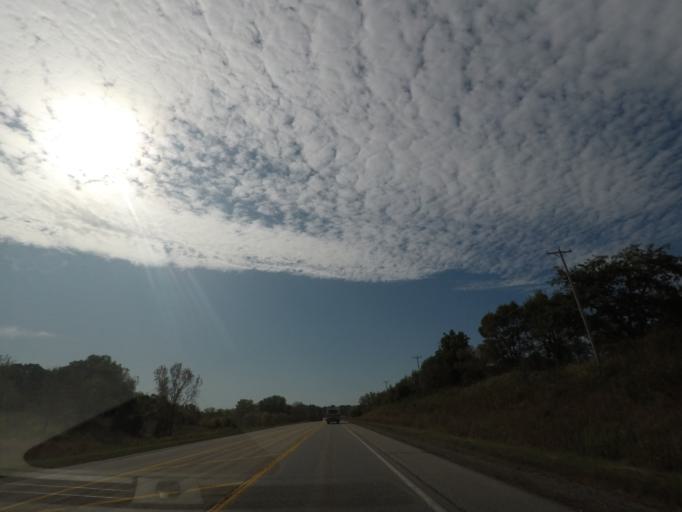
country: US
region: Iowa
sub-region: Story County
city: Ames
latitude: 42.0748
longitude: -93.6213
